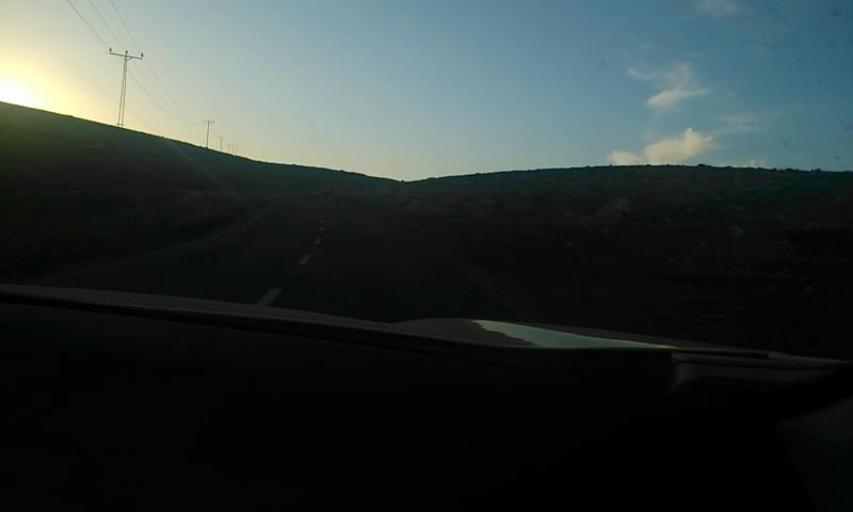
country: PS
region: West Bank
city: Rammun
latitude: 31.9177
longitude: 35.3381
